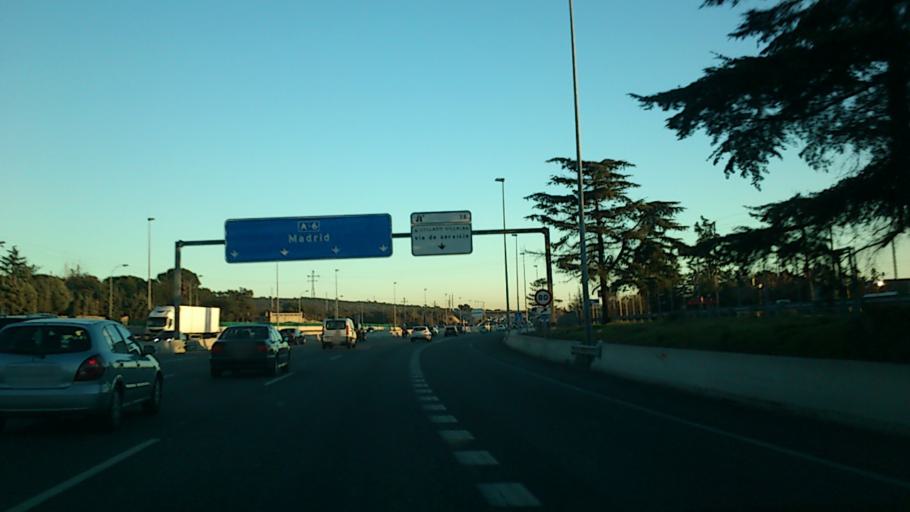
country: ES
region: Madrid
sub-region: Provincia de Madrid
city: Collado-Villalba
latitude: 40.6287
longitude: -3.9959
